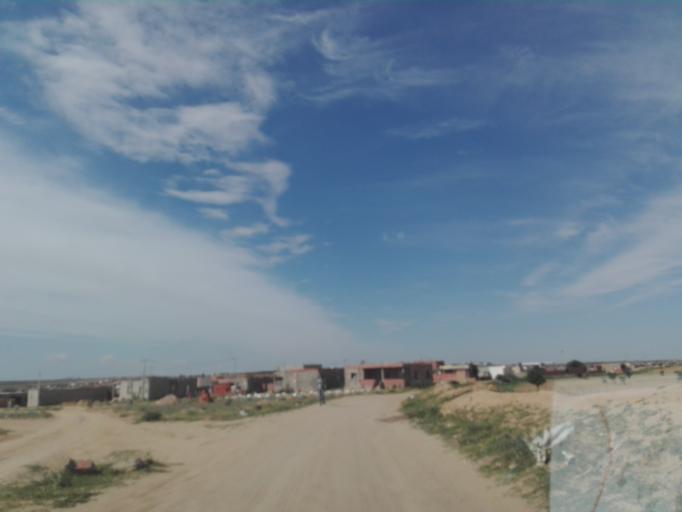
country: TN
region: Safaqis
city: Sfax
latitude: 34.7433
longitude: 10.5105
